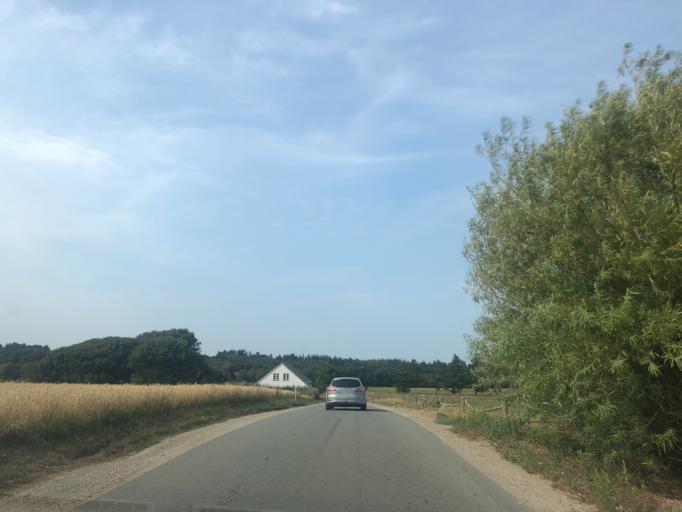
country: DK
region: North Denmark
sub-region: Morso Kommune
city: Nykobing Mors
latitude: 56.8308
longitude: 9.0429
